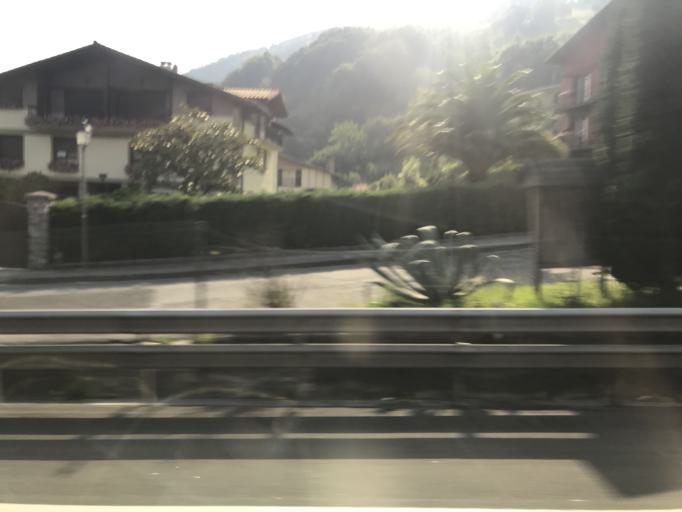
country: ES
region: Basque Country
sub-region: Provincia de Guipuzcoa
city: Irura
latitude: 43.1667
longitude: -2.0661
